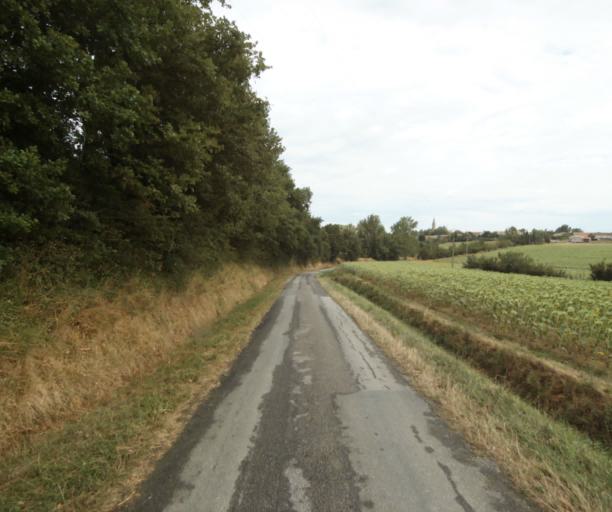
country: FR
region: Midi-Pyrenees
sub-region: Departement de la Haute-Garonne
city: Revel
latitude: 43.4313
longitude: 1.9668
